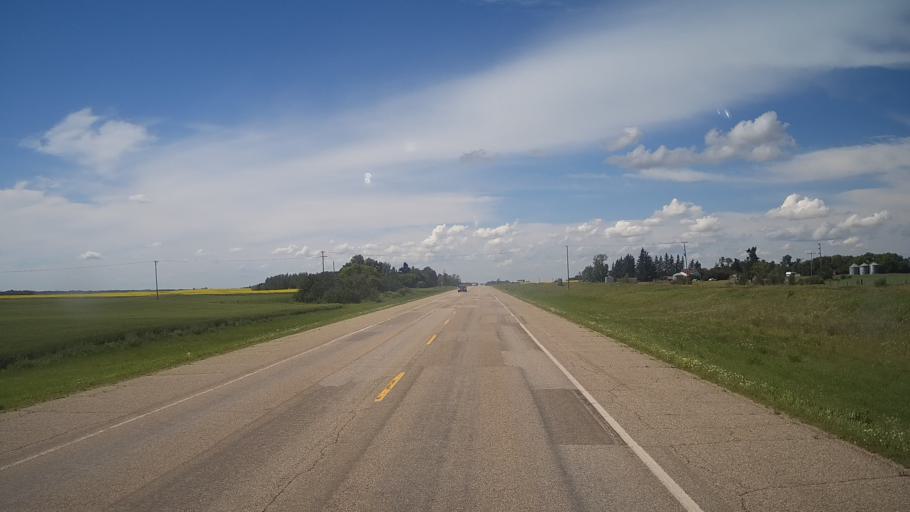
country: CA
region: Saskatchewan
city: Yorkton
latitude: 51.0890
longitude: -102.2591
